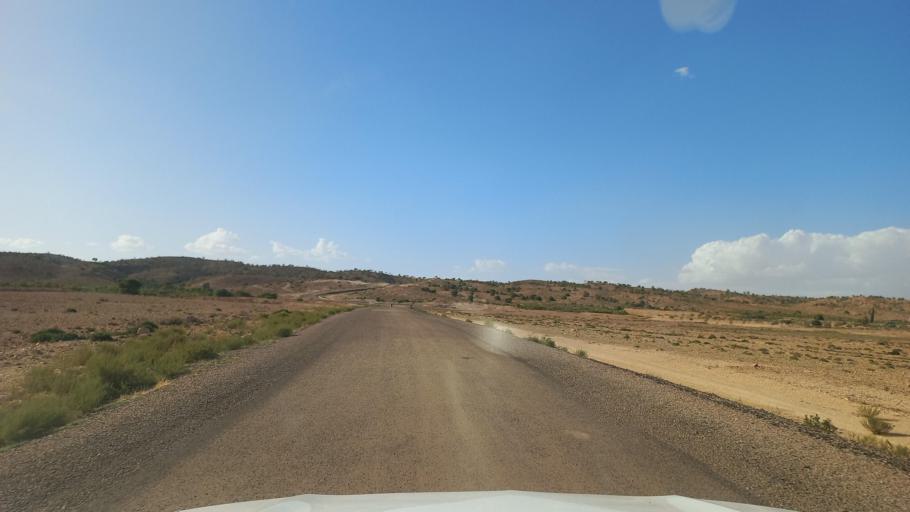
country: TN
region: Al Qasrayn
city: Sbiba
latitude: 35.3530
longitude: 8.9855
